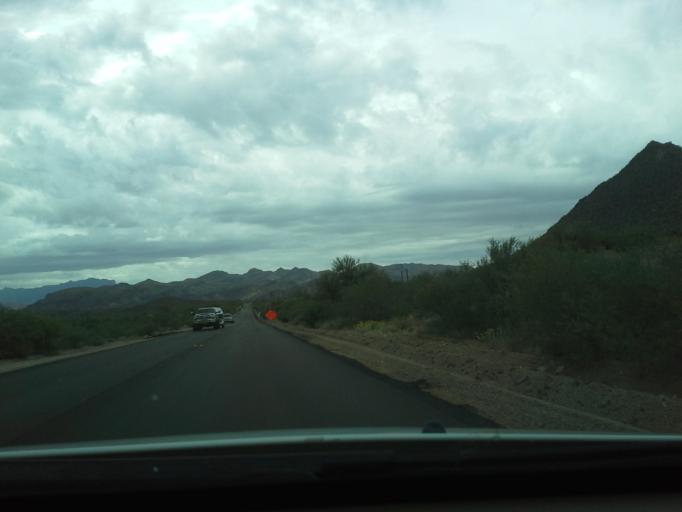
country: US
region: Arizona
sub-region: Maricopa County
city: Fountain Hills
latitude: 33.5989
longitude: -111.5456
